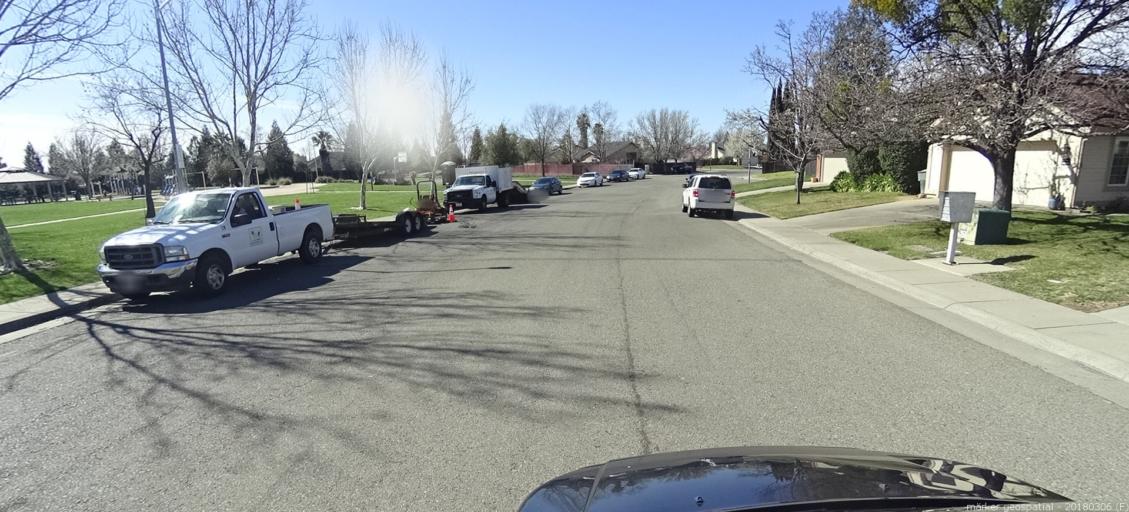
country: US
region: California
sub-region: Sacramento County
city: Vineyard
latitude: 38.4600
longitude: -121.3552
